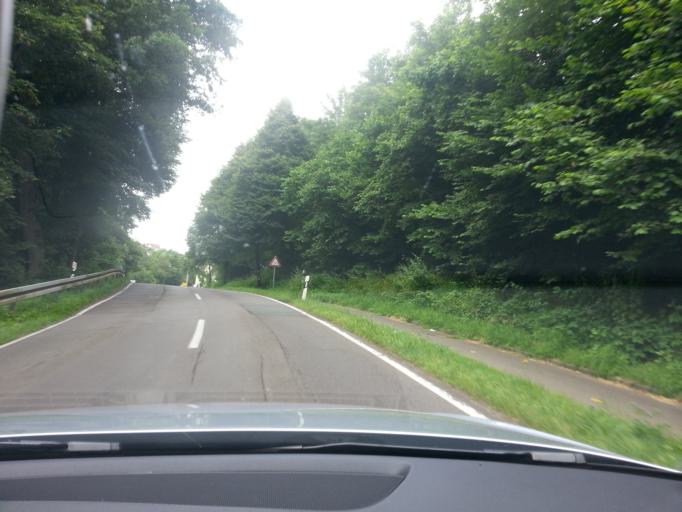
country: DE
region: Saarland
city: Marpingen
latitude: 49.4441
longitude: 7.0494
